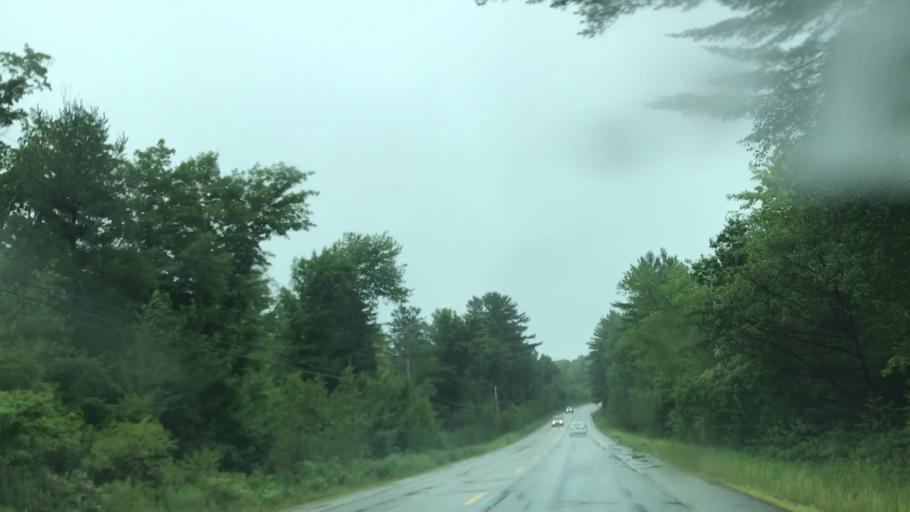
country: US
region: Maine
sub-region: York County
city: North Berwick
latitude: 43.2995
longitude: -70.7692
